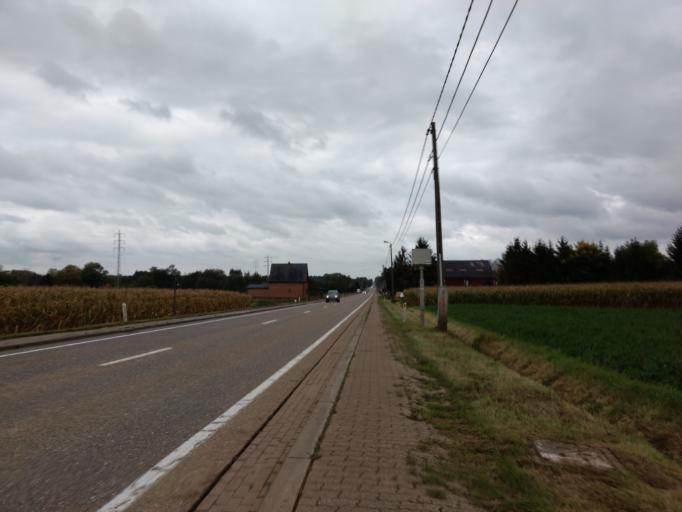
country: BE
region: Flanders
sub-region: Provincie Vlaams-Brabant
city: Bekkevoort
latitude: 50.9319
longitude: 4.9881
